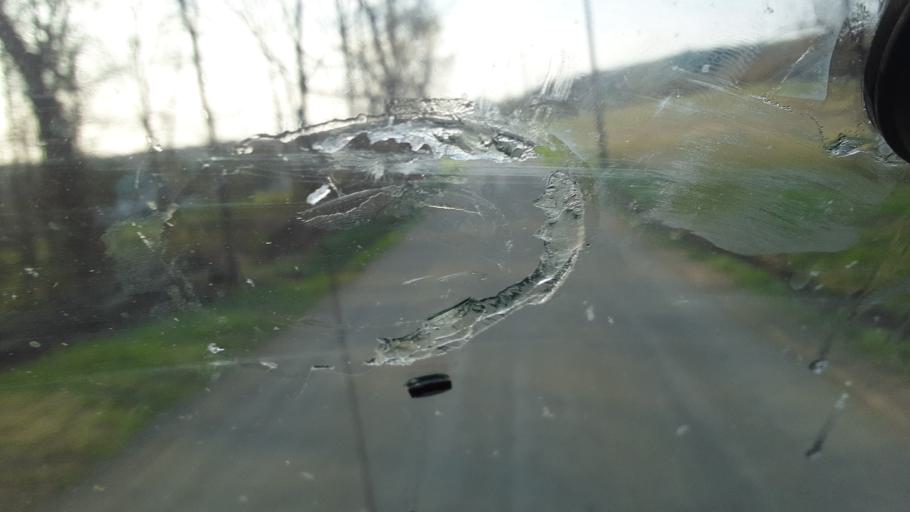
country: US
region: Ohio
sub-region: Richland County
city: Lincoln Heights
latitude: 40.7196
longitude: -82.4378
